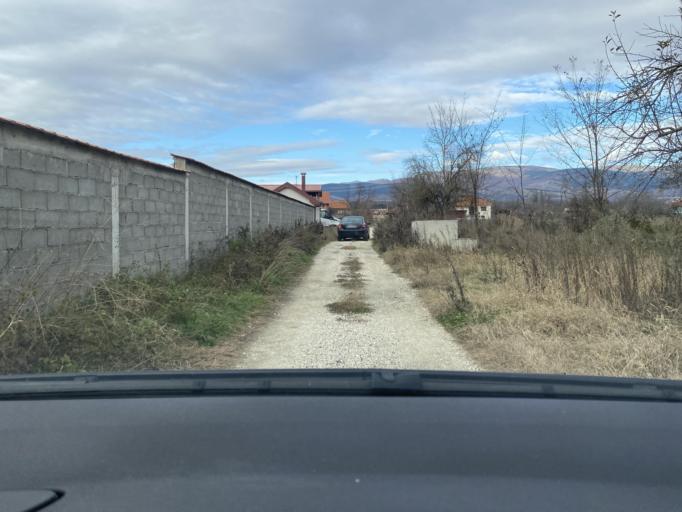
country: MK
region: Opstina Rankovce
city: Rankovce
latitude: 42.1674
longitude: 22.1575
